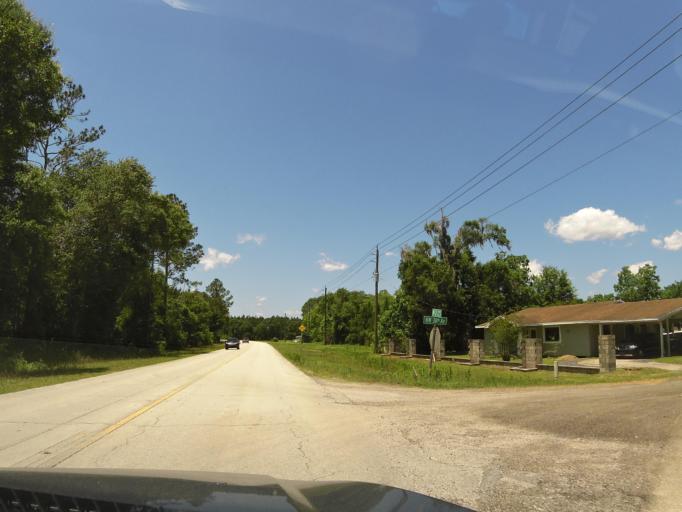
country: US
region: Florida
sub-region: Bradford County
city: Starke
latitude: 30.0485
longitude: -82.1084
